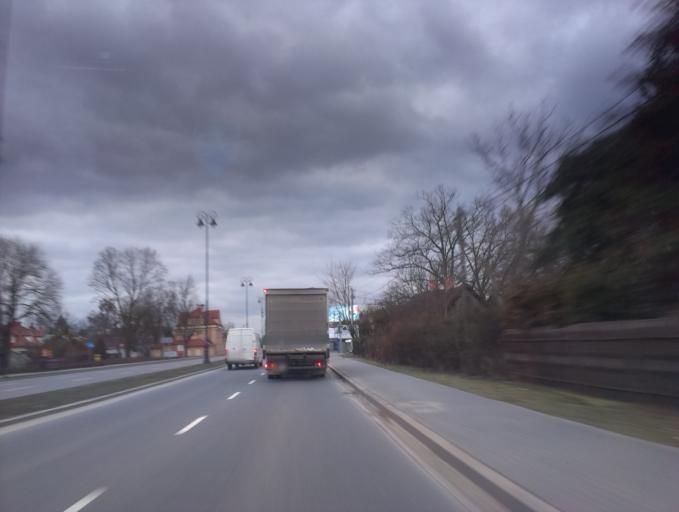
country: PL
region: Masovian Voivodeship
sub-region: Powiat piaseczynski
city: Konstancin-Jeziorna
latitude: 52.1047
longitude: 21.1137
